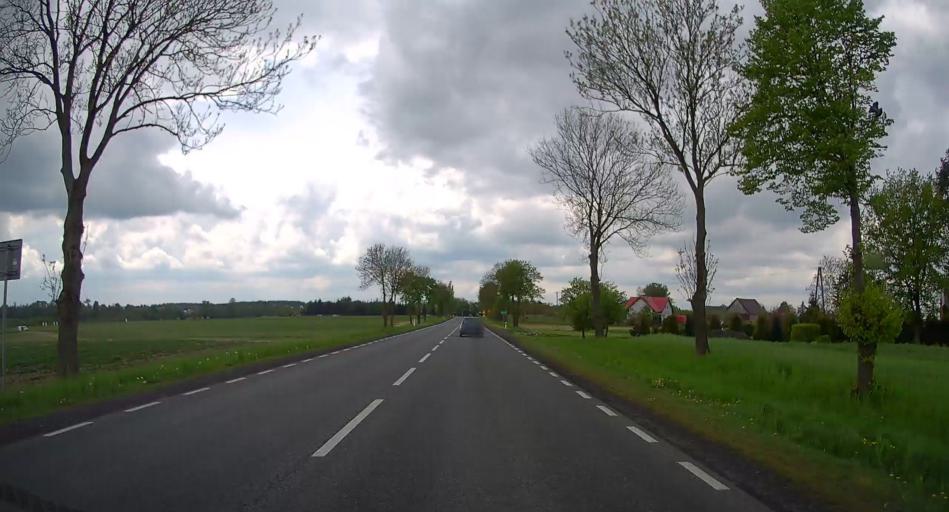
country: PL
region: Masovian Voivodeship
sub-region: Powiat plonski
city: Zaluski
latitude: 52.4356
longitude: 20.4731
